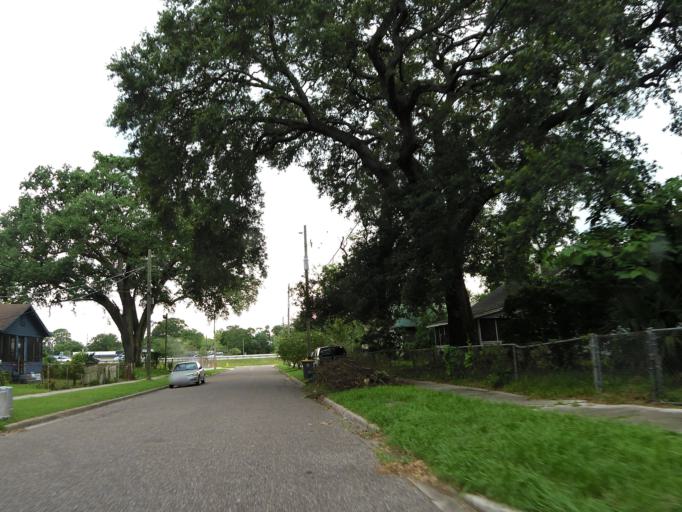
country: US
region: Florida
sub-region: Duval County
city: Jacksonville
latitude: 30.3515
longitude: -81.6354
